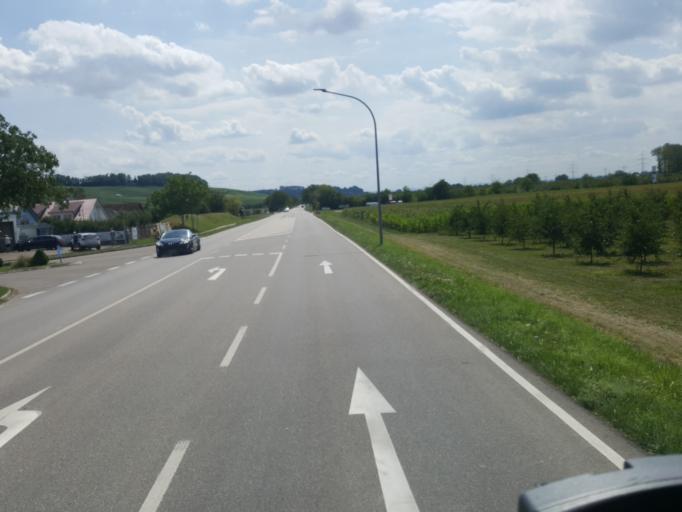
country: DE
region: Baden-Wuerttemberg
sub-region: Freiburg Region
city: Auggen
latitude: 47.7873
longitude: 7.5899
